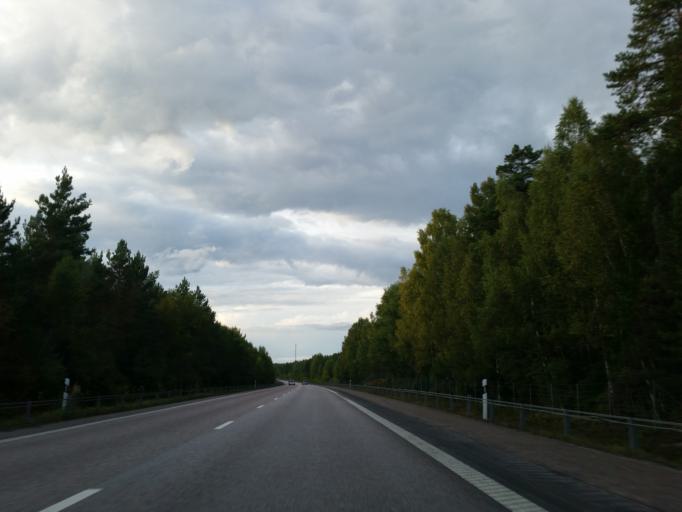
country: SE
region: Stockholm
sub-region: Sigtuna Kommun
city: Marsta
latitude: 59.6553
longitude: 17.8880
